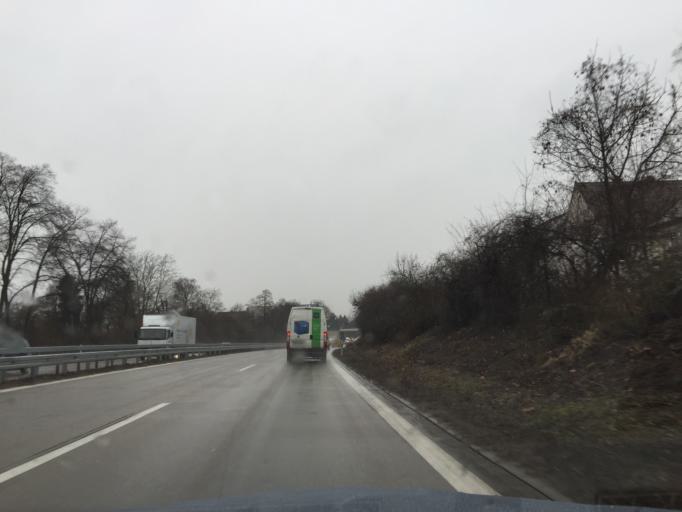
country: DE
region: Baden-Wuerttemberg
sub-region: Karlsruhe Region
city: Heidelberg
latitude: 49.4084
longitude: 8.6662
